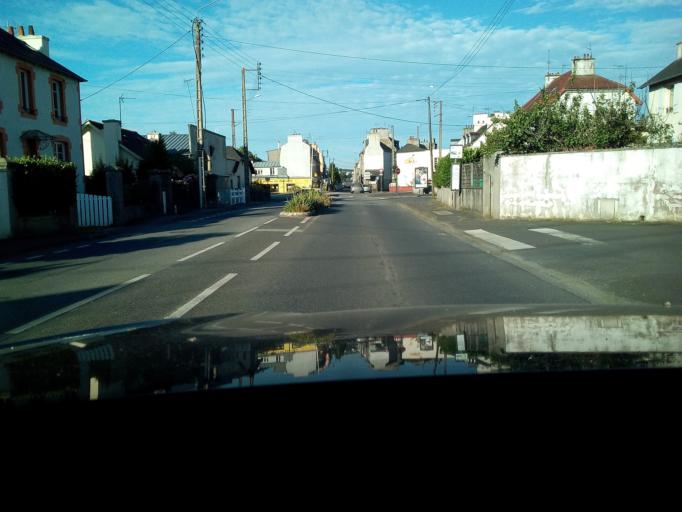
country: FR
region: Brittany
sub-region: Departement du Finistere
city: Landerneau
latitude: 48.4546
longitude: -4.2440
